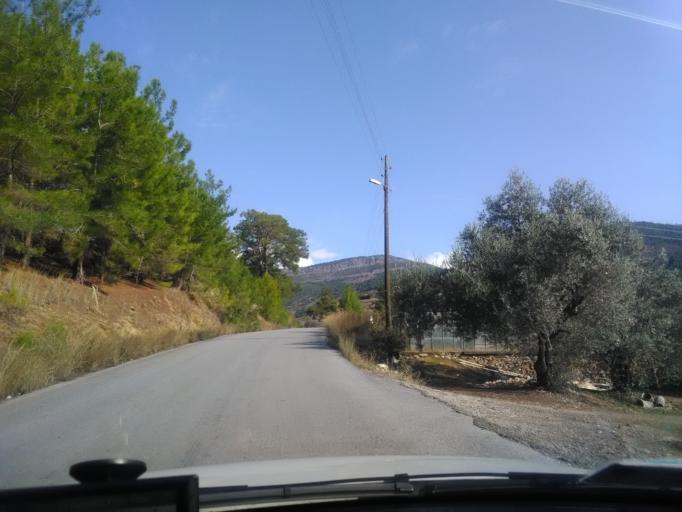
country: TR
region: Antalya
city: Gazipasa
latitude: 36.2943
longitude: 32.3303
